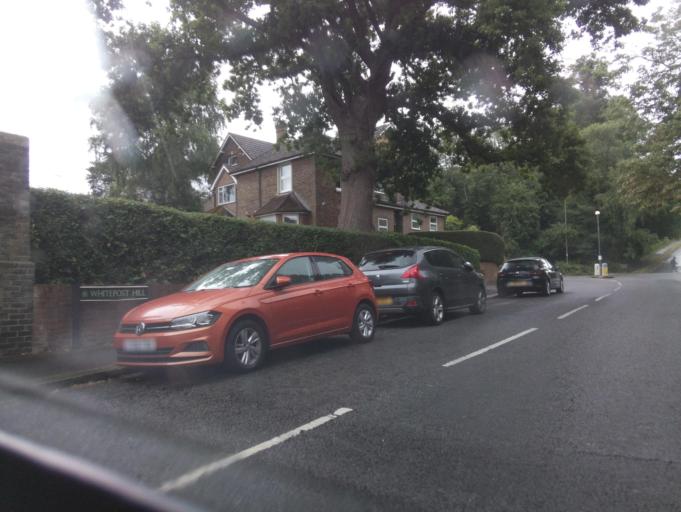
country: GB
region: England
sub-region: Surrey
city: Redhill
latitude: 51.2369
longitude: -0.1817
